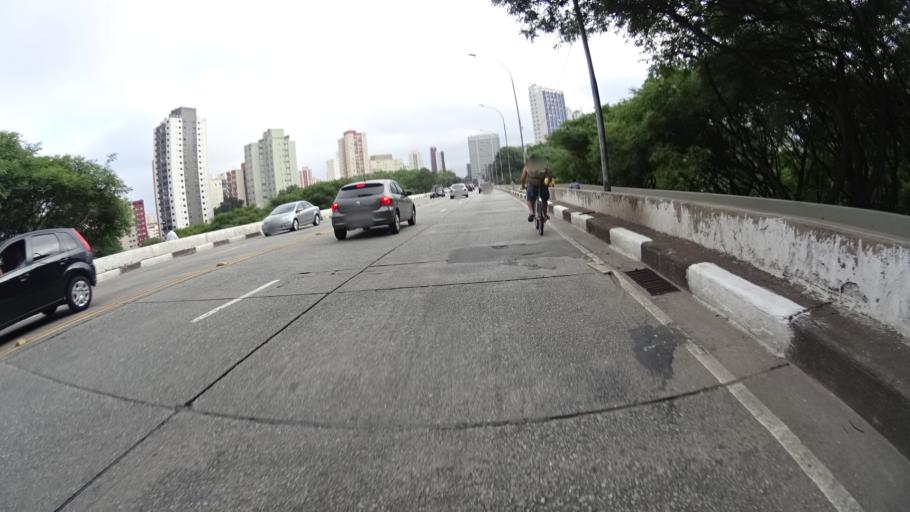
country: BR
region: Sao Paulo
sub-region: Diadema
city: Diadema
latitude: -23.6284
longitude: -46.6414
